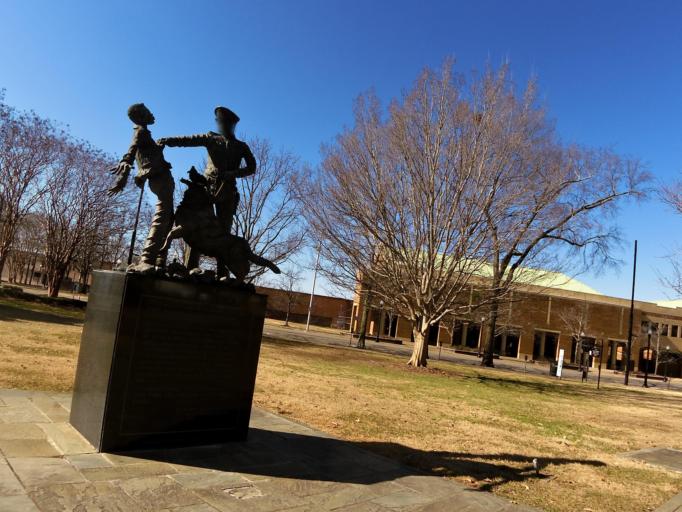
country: US
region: Alabama
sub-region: Jefferson County
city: Birmingham
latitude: 33.5160
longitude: -86.8137
